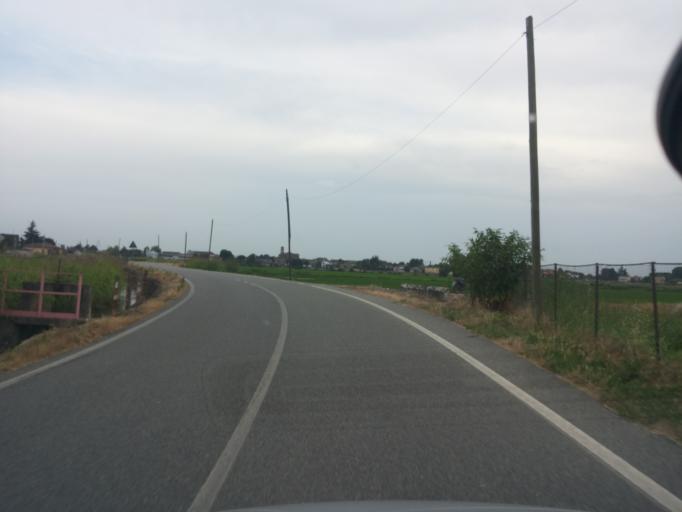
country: IT
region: Piedmont
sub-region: Provincia di Vercelli
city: Pezzana
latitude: 45.2697
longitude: 8.4825
